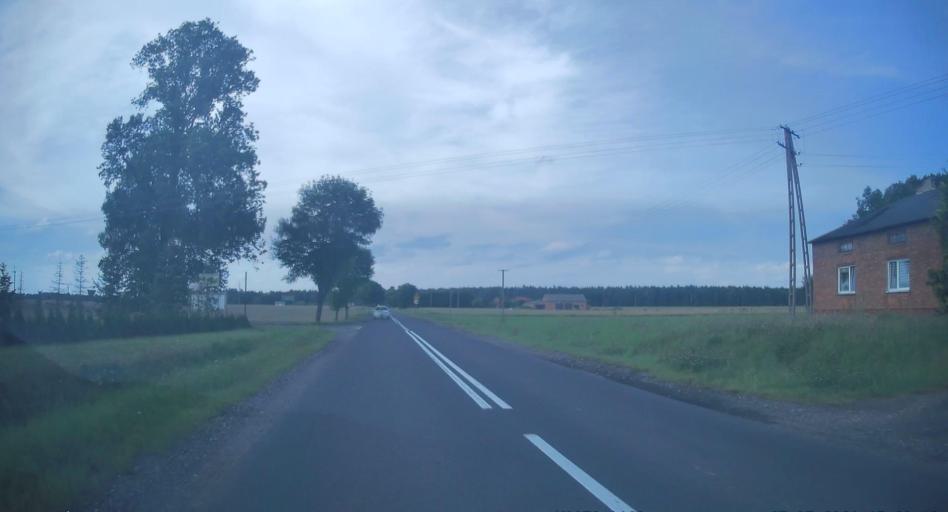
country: PL
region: Lodz Voivodeship
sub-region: Powiat tomaszowski
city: Rzeczyca
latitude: 51.6769
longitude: 20.2663
